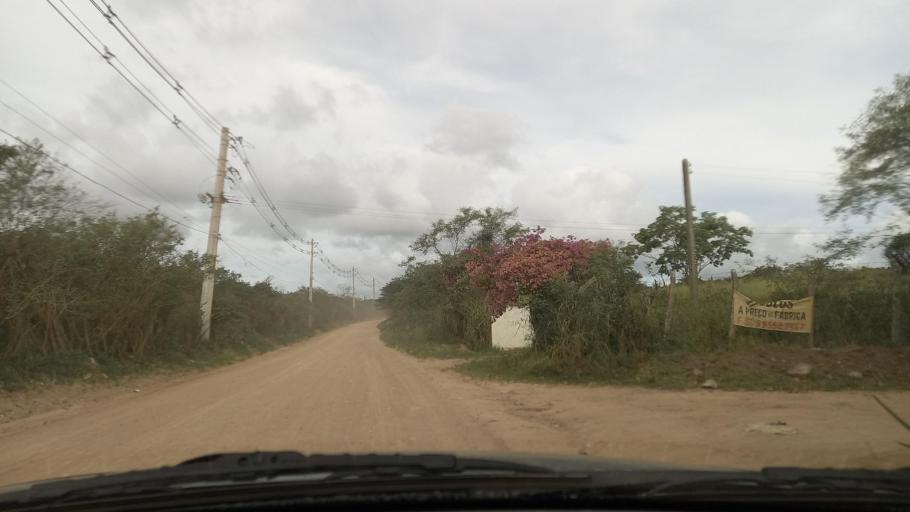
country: BR
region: Pernambuco
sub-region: Gravata
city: Gravata
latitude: -8.1970
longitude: -35.5379
